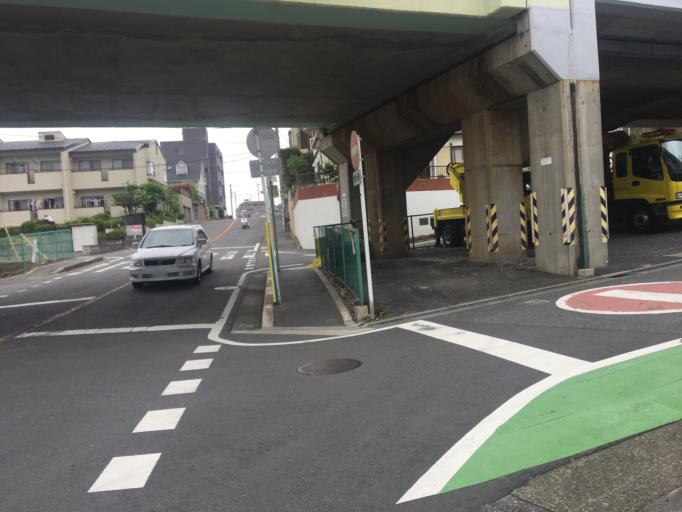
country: JP
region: Saitama
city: Shimotoda
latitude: 35.8456
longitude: 139.6646
